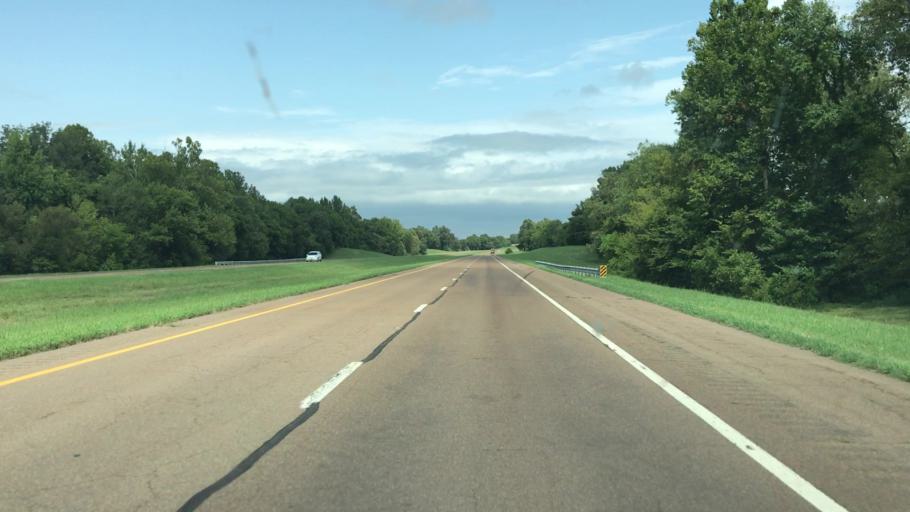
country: US
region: Tennessee
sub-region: Obion County
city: South Fulton
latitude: 36.4709
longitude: -88.9669
